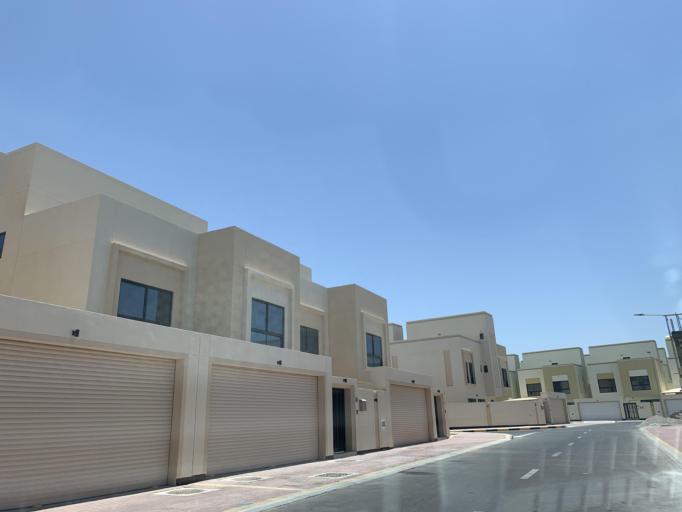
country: BH
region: Manama
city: Jidd Hafs
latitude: 26.2328
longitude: 50.4973
